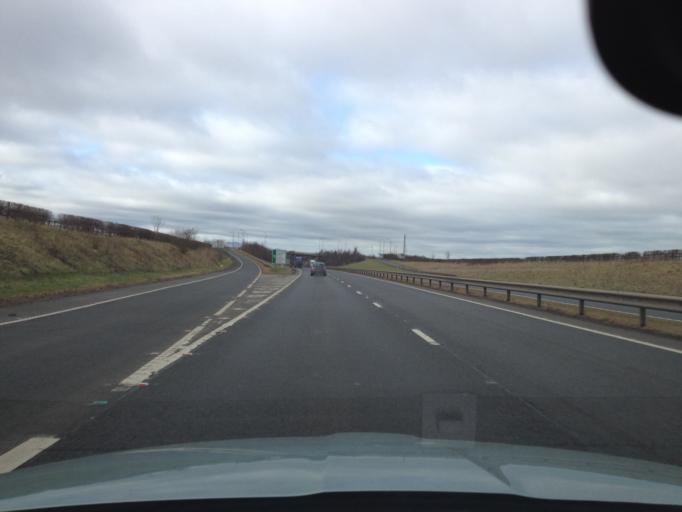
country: GB
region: Scotland
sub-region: East Lothian
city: Longniddry
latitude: 55.9511
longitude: -2.8740
